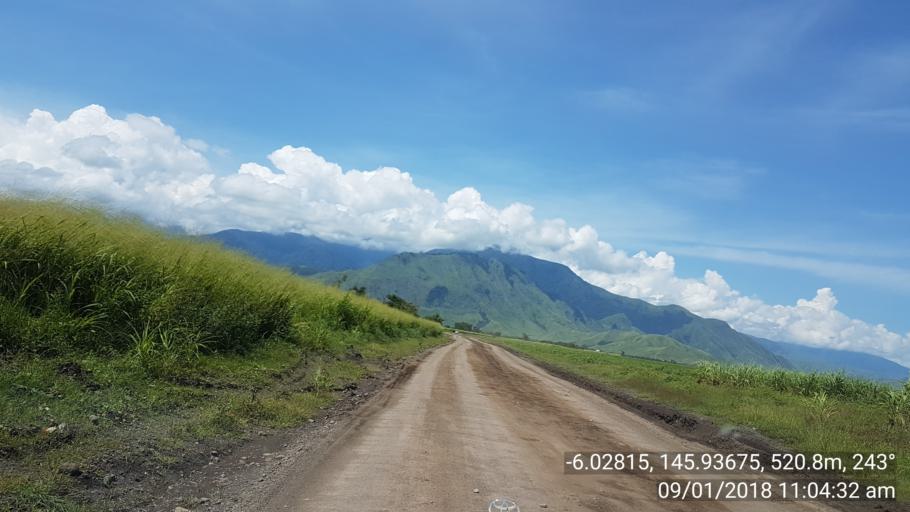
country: PG
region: Eastern Highlands
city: Kainantu
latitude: -6.0280
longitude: 145.9370
